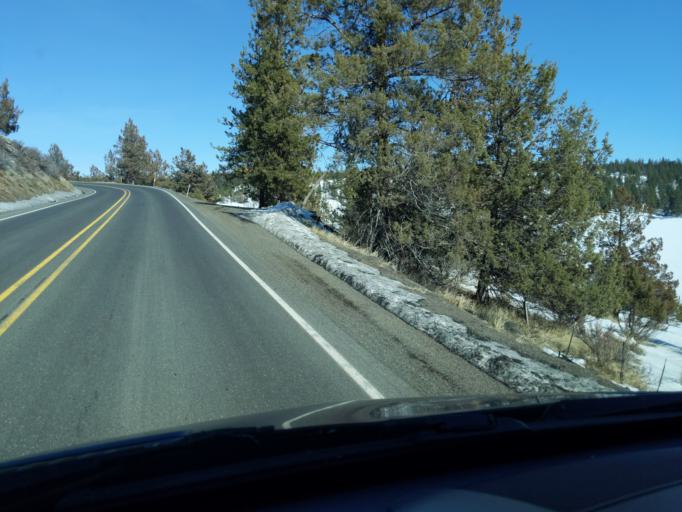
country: US
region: Oregon
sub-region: Grant County
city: John Day
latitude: 44.9042
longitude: -119.0122
